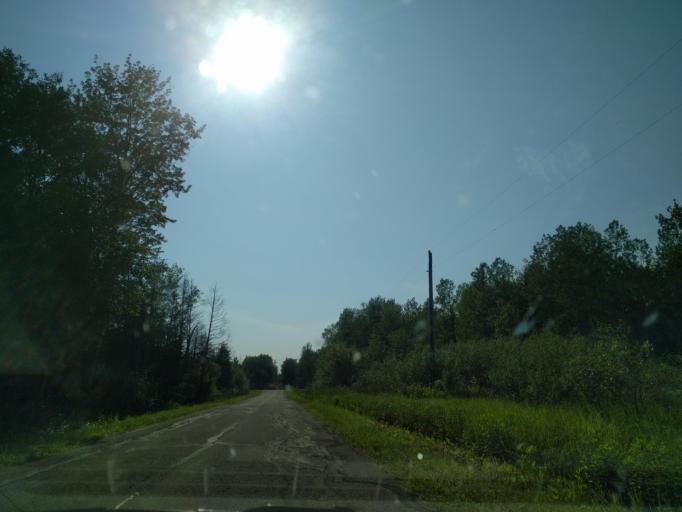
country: US
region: Michigan
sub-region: Delta County
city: Gladstone
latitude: 45.8910
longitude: -87.0634
